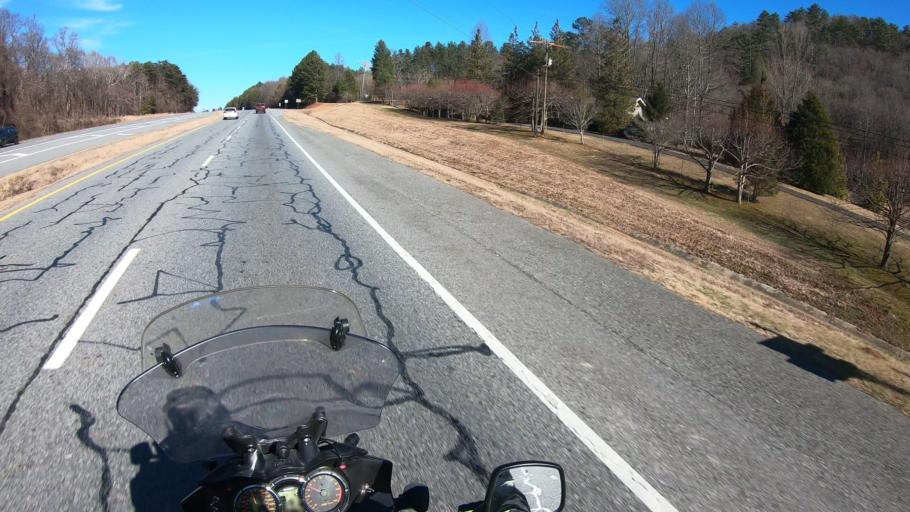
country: US
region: Georgia
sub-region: Gilmer County
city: Ellijay
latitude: 34.7711
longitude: -84.3965
